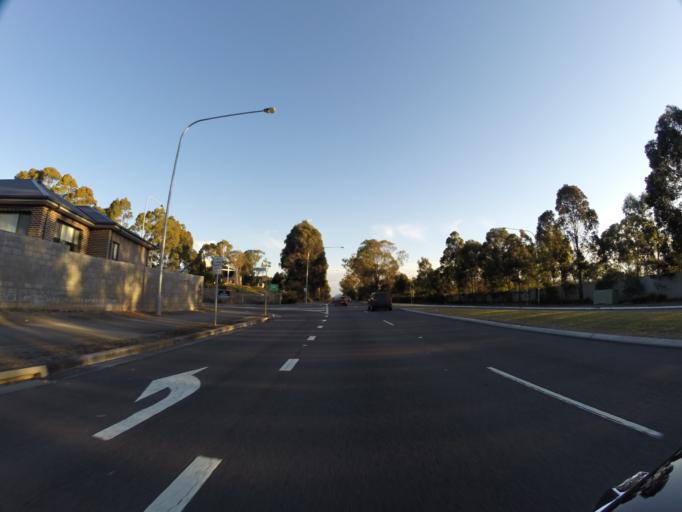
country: AU
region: New South Wales
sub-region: Fairfield
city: Cecil Park
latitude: -33.8860
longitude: 150.8629
